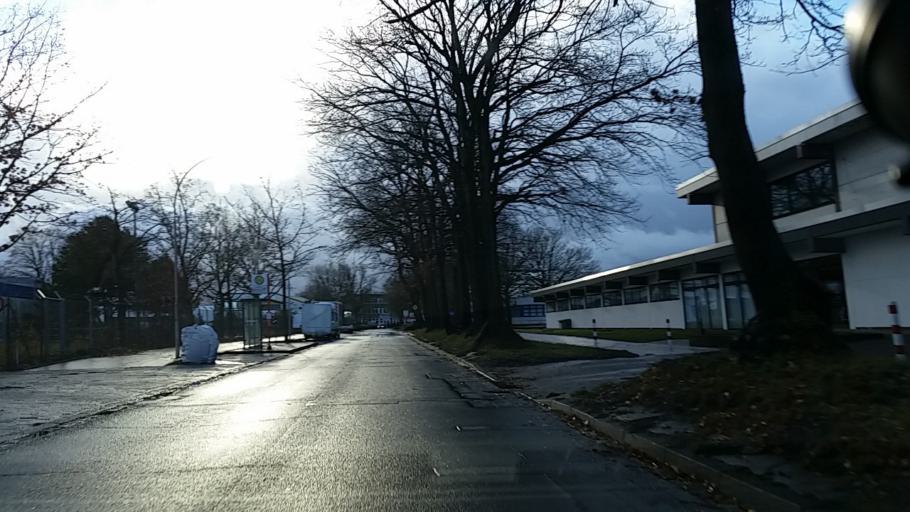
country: DE
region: Schleswig-Holstein
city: Halstenbek
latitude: 53.5938
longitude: 9.8351
